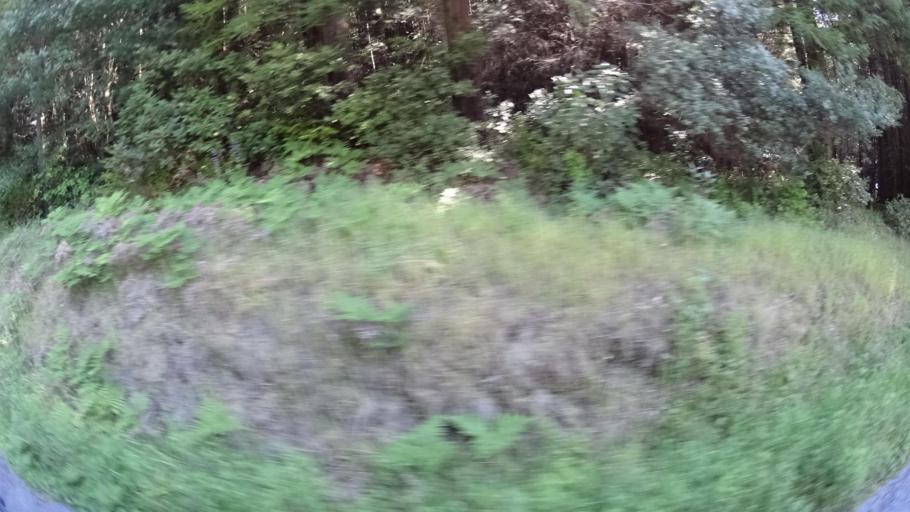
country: US
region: California
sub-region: Humboldt County
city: Rio Dell
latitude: 40.4446
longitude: -123.9750
